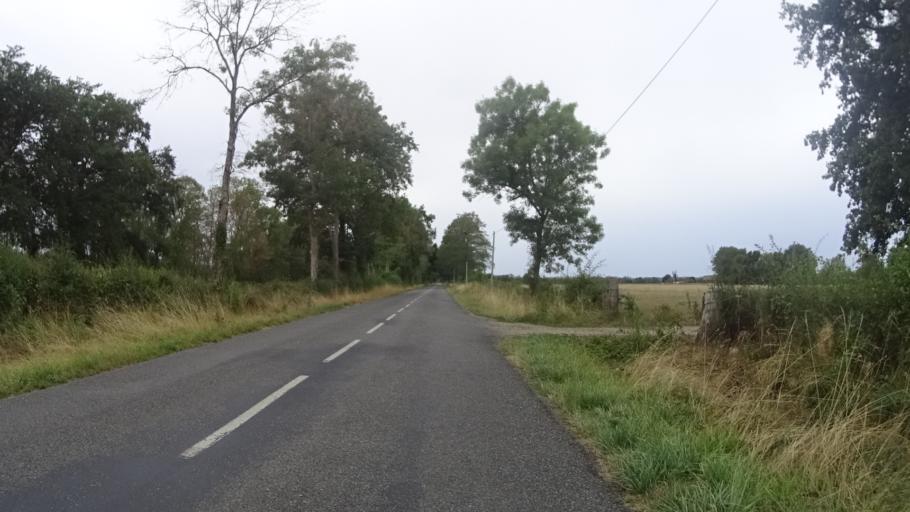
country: FR
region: Bourgogne
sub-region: Departement de la Nievre
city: Decize
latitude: 46.7932
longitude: 3.5085
